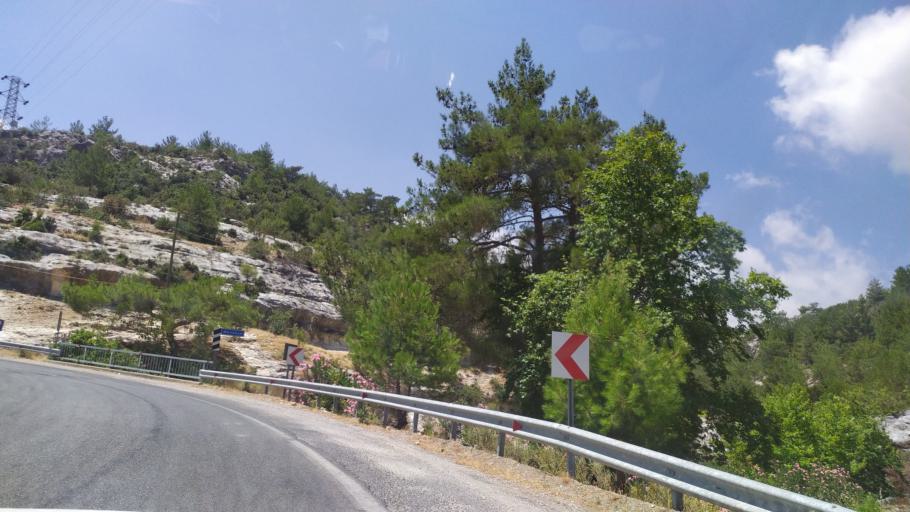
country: TR
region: Mersin
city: Gulnar
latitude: 36.2781
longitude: 33.3795
